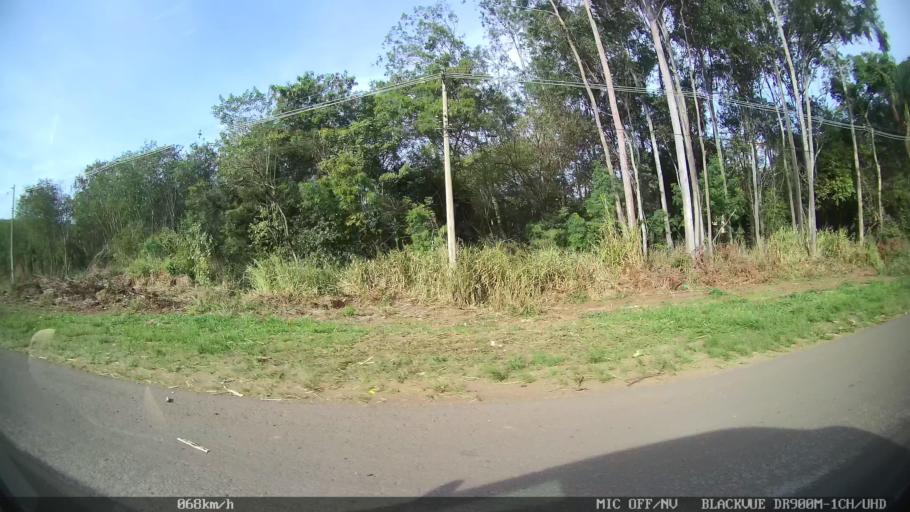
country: BR
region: Sao Paulo
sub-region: Piracicaba
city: Piracicaba
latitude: -22.6827
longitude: -47.6896
